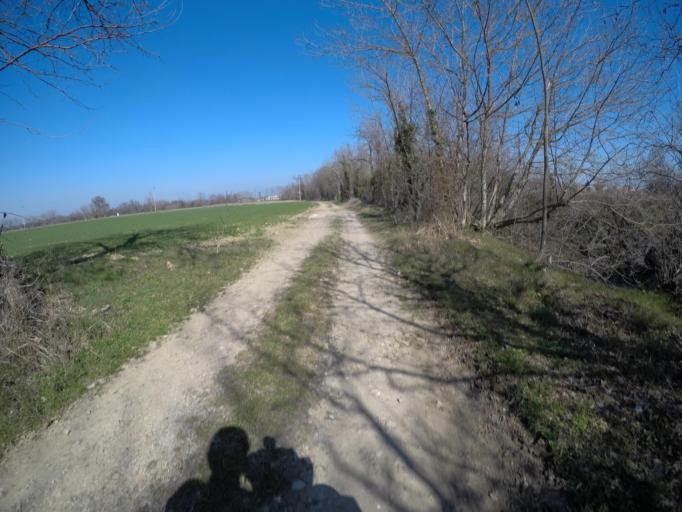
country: IT
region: Friuli Venezia Giulia
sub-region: Provincia di Udine
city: Zugliano-Terenzano-Cargnacco
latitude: 46.0152
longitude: 13.2026
